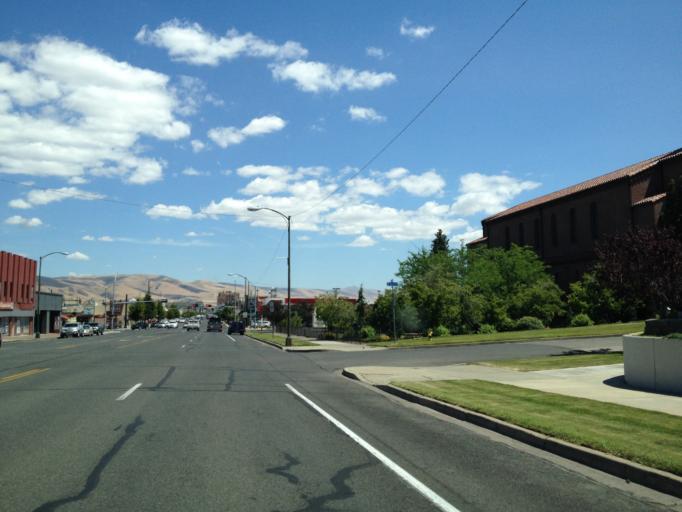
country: US
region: Washington
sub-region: Yakima County
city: Yakima
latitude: 46.5988
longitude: -120.5206
